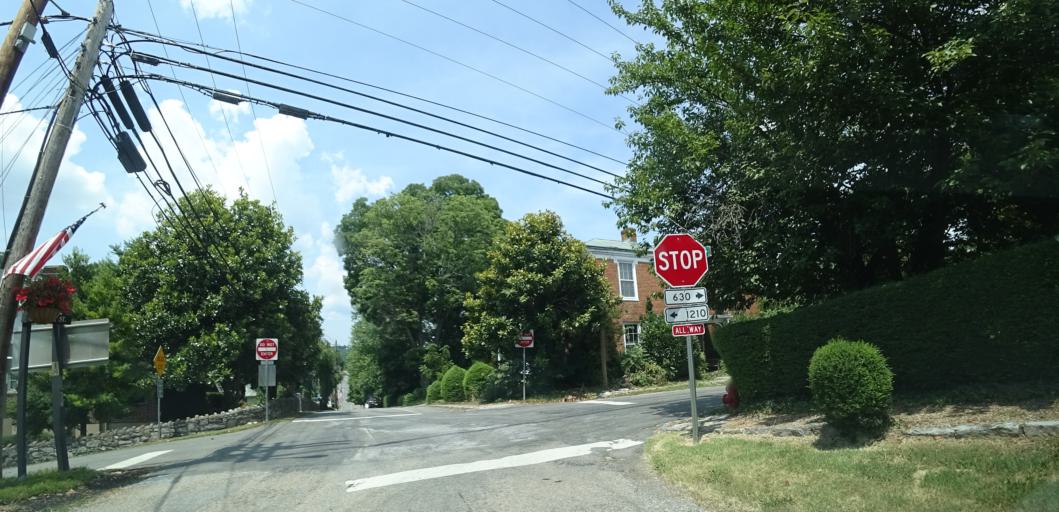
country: US
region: Virginia
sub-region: Botetourt County
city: Fincastle
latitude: 37.4992
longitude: -79.8724
